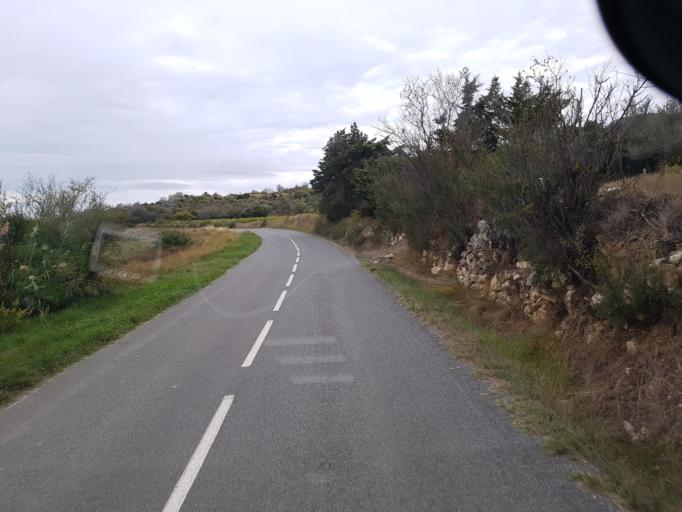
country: FR
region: Languedoc-Roussillon
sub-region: Departement de l'Aude
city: Peyriac-de-Mer
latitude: 43.1317
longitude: 2.9862
